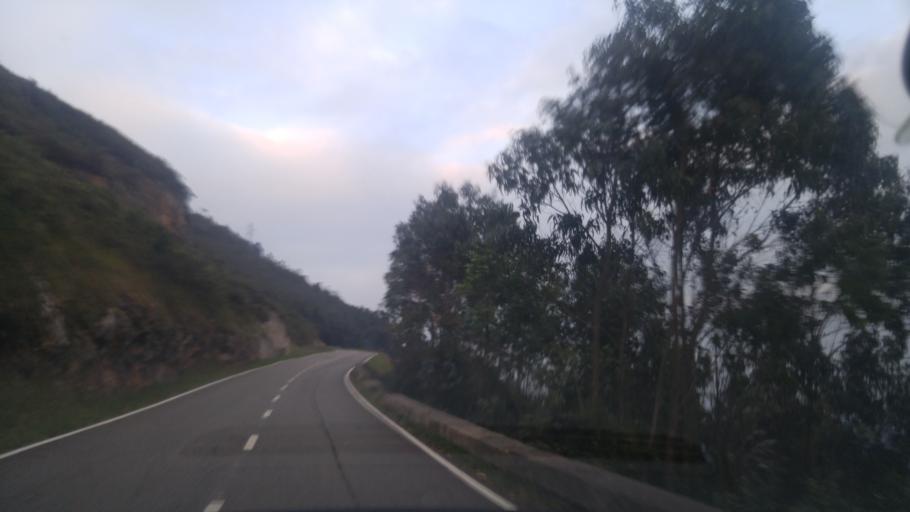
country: ES
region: Asturias
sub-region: Province of Asturias
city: Oviedo
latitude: 43.3812
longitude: -5.8580
